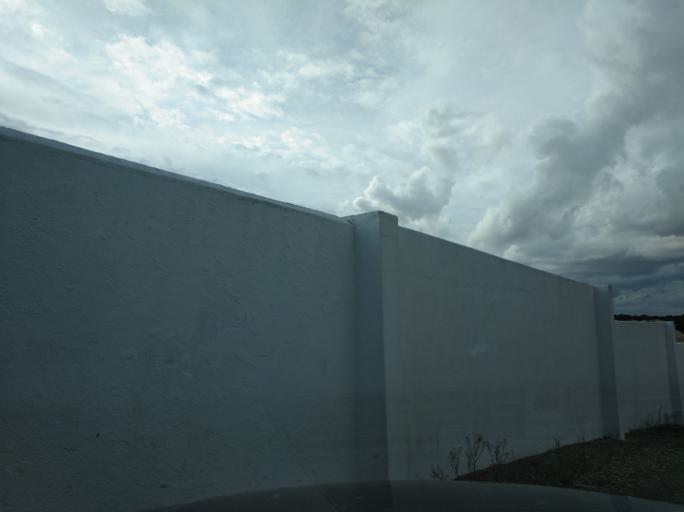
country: PT
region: Portalegre
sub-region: Campo Maior
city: Campo Maior
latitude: 39.0606
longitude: -7.1242
